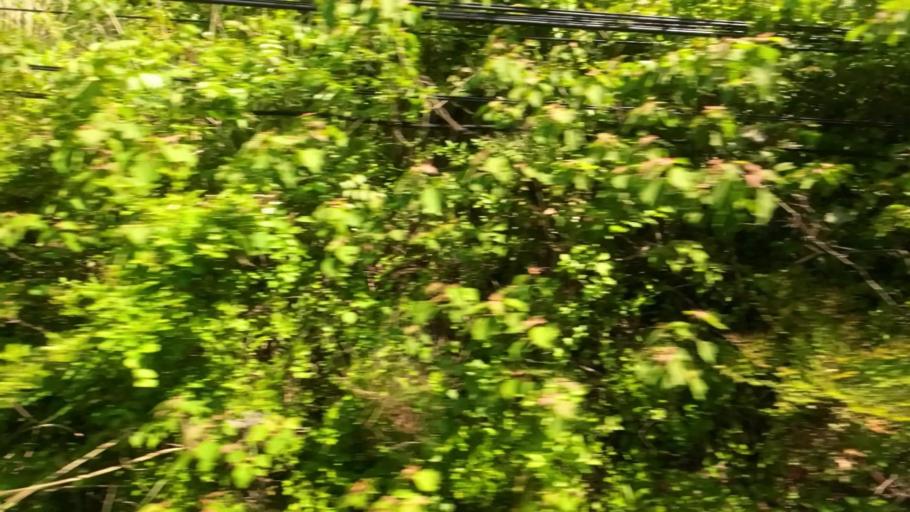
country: JP
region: Ehime
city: Saijo
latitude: 33.9222
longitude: 133.2344
